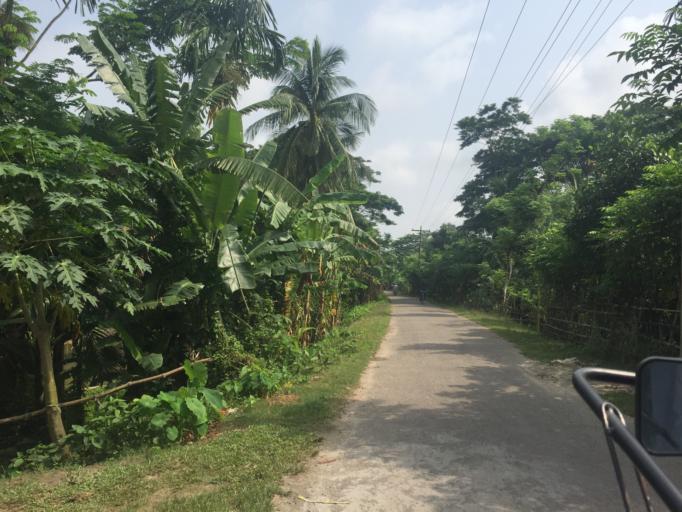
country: BD
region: Barisal
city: Mathba
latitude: 22.2318
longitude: 89.9157
